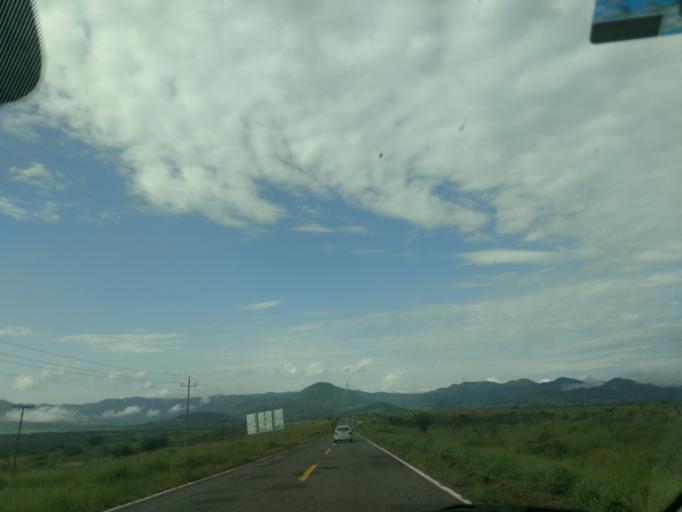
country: MX
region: Jalisco
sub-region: Atengo
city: Soyatlan del Oro
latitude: 20.5395
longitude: -104.3112
